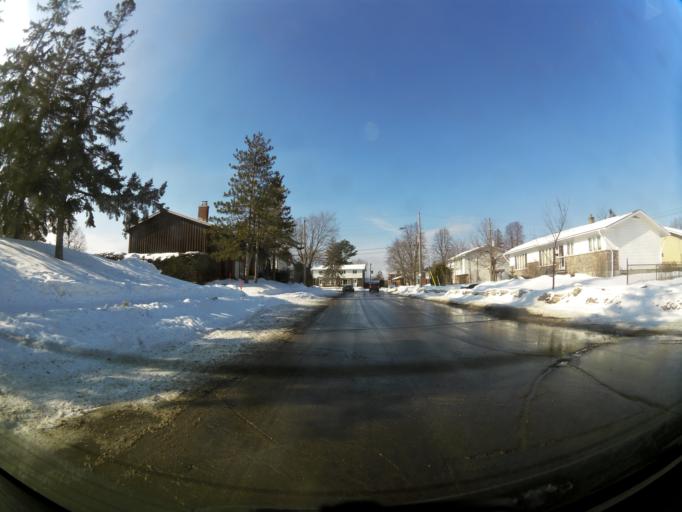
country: CA
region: Ontario
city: Ottawa
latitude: 45.3894
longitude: -75.6252
